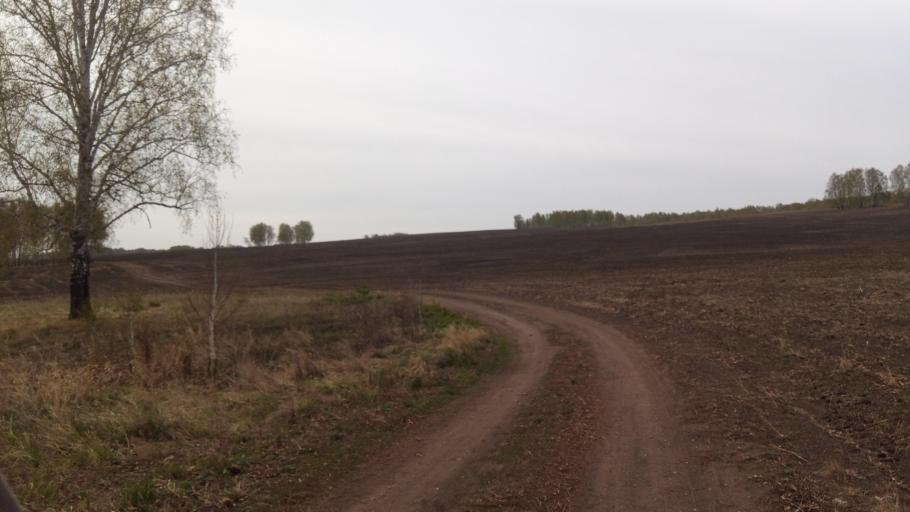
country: RU
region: Chelyabinsk
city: Timiryazevskiy
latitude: 55.0218
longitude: 60.8517
